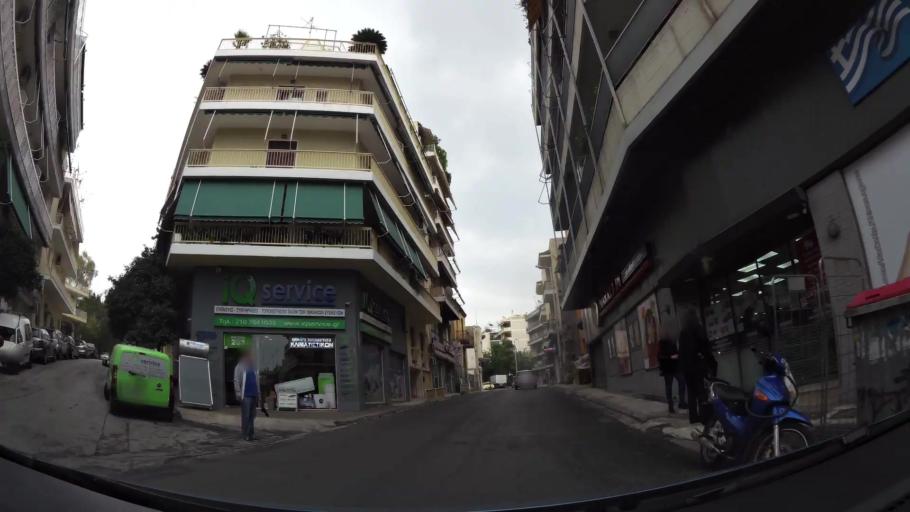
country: GR
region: Attica
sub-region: Nomarchia Athinas
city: Kaisariani
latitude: 37.9602
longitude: 23.7607
